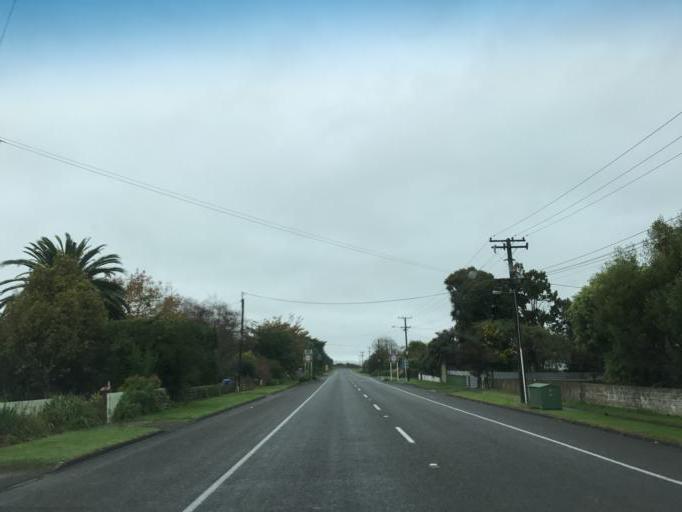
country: NZ
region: Taranaki
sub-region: South Taranaki District
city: Patea
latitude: -39.7636
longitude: 174.6382
